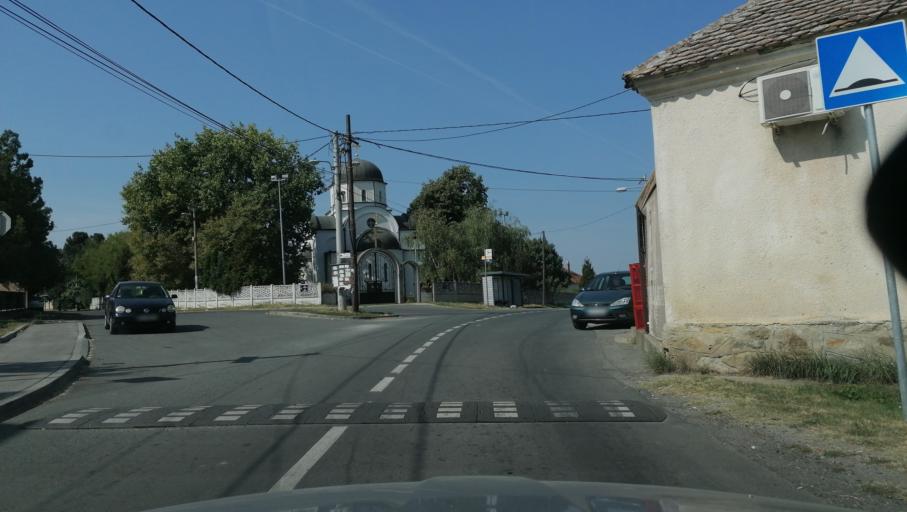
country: RS
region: Central Serbia
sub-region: Belgrade
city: Zvezdara
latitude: 44.7018
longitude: 20.5534
